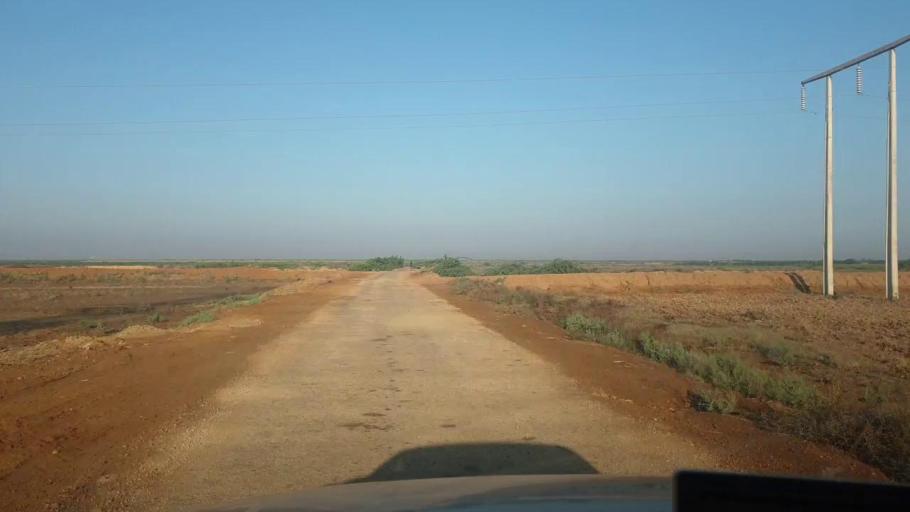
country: PK
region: Sindh
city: Thatta
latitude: 24.7009
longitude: 67.8533
